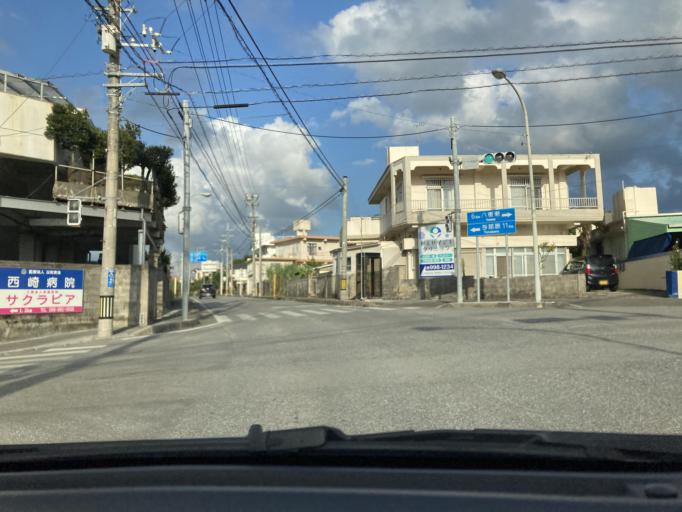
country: JP
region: Okinawa
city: Itoman
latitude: 26.1371
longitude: 127.6982
